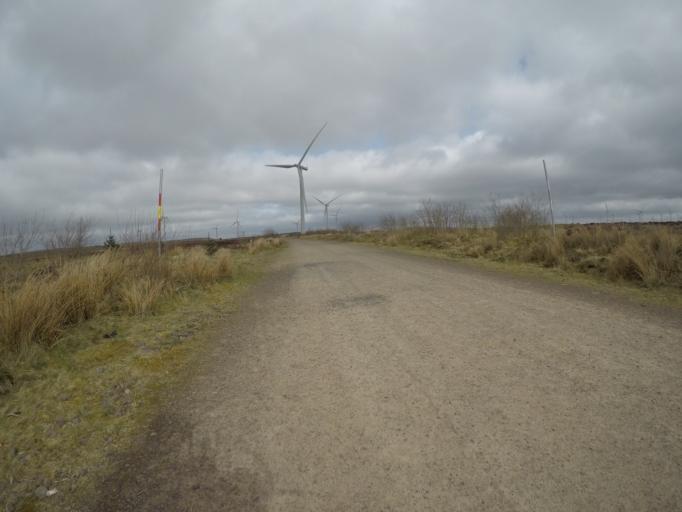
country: GB
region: Scotland
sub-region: East Renfrewshire
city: Newton Mearns
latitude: 55.6986
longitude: -4.3432
